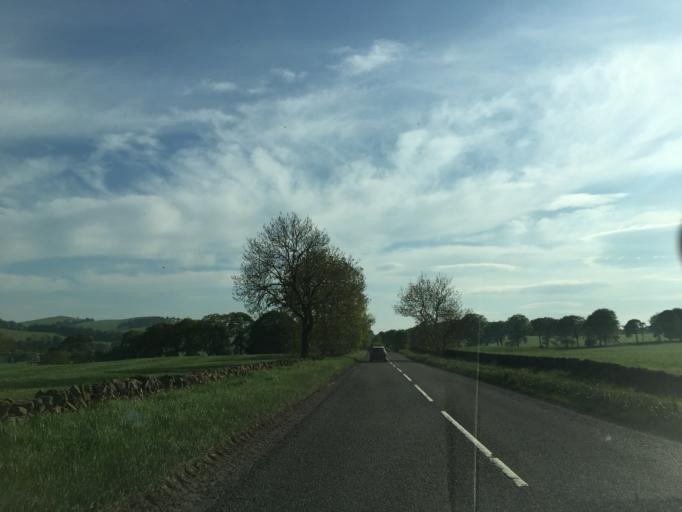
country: GB
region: Scotland
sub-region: The Scottish Borders
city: West Linton
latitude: 55.7148
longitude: -3.3450
